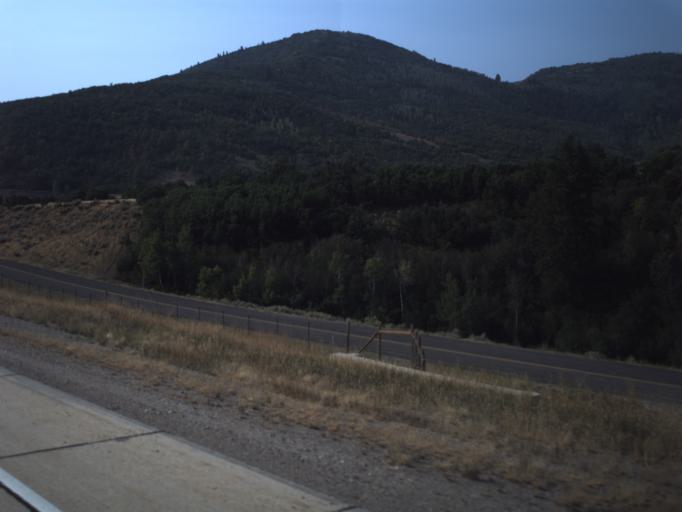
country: US
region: Utah
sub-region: Summit County
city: Park City
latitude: 40.6211
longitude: -111.4383
